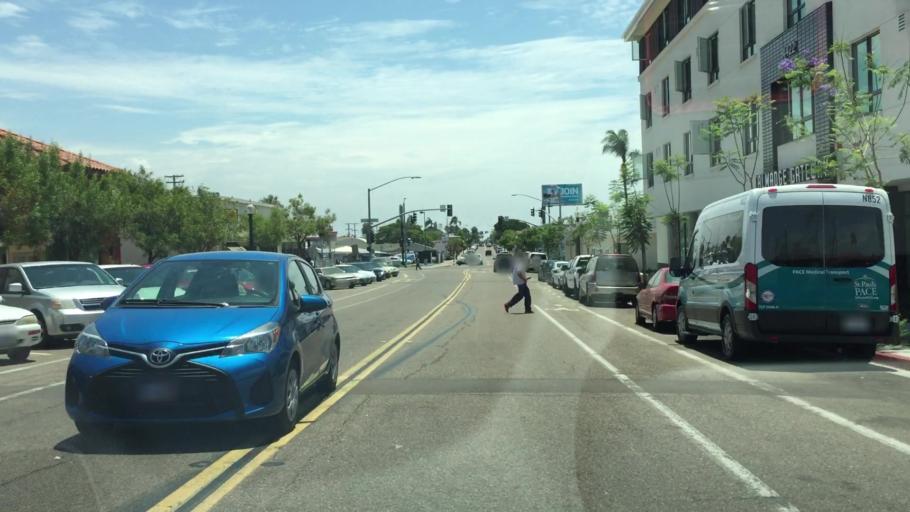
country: US
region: California
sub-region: San Diego County
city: Lemon Grove
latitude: 32.7571
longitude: -117.0922
